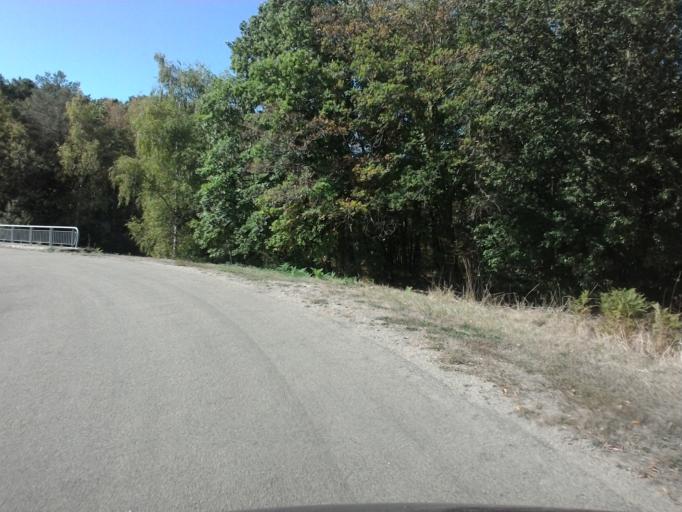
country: FR
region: Bourgogne
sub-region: Departement de la Cote-d'Or
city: Semur-en-Auxois
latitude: 47.4705
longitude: 4.3535
